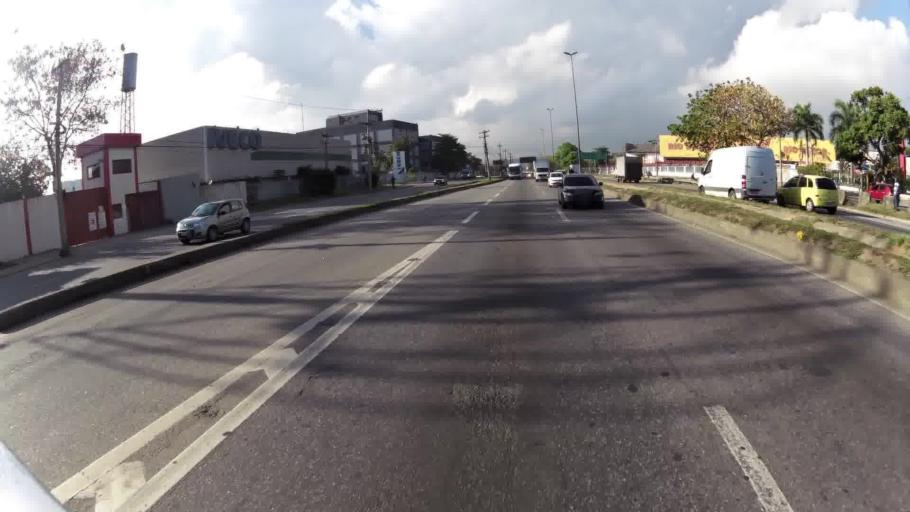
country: BR
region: Rio de Janeiro
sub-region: Duque De Caxias
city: Duque de Caxias
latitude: -22.8114
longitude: -43.2882
